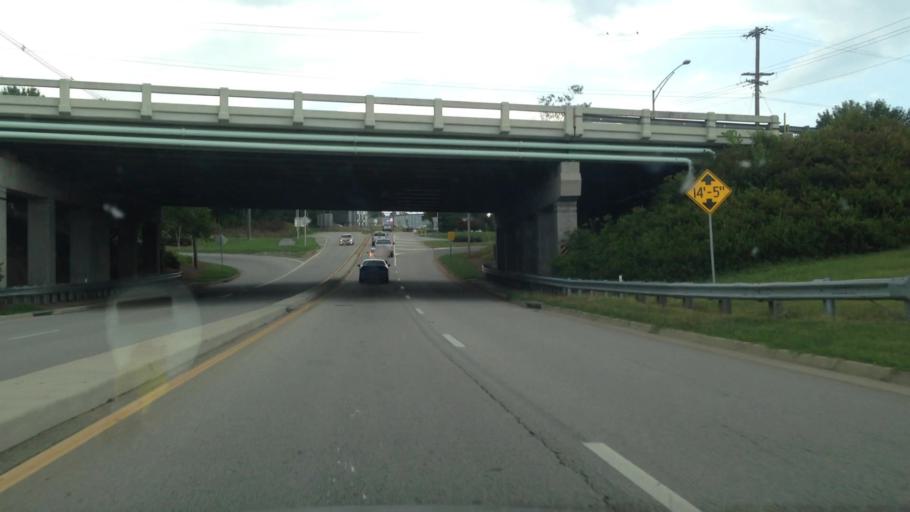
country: US
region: Virginia
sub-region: City of Danville
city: Danville
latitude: 36.5807
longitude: -79.4324
